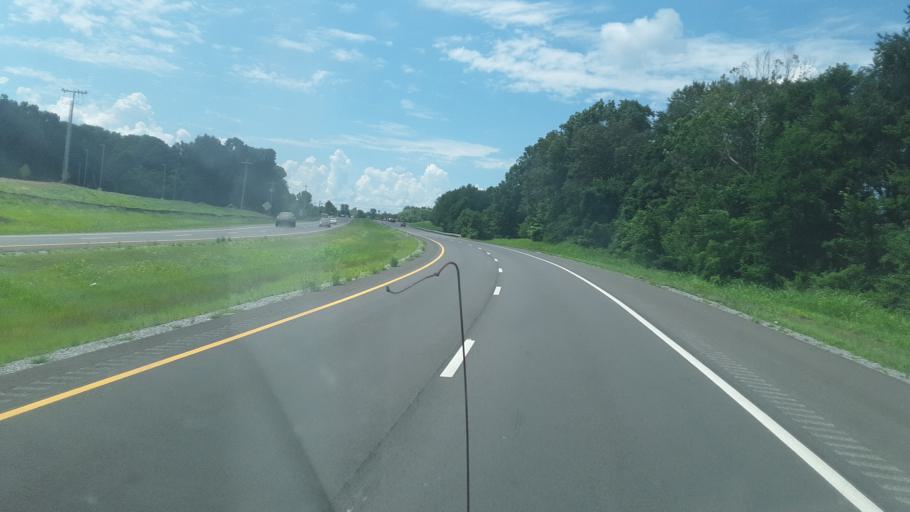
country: US
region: Kentucky
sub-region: Christian County
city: Fort Campbell North
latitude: 36.5805
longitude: -87.4445
